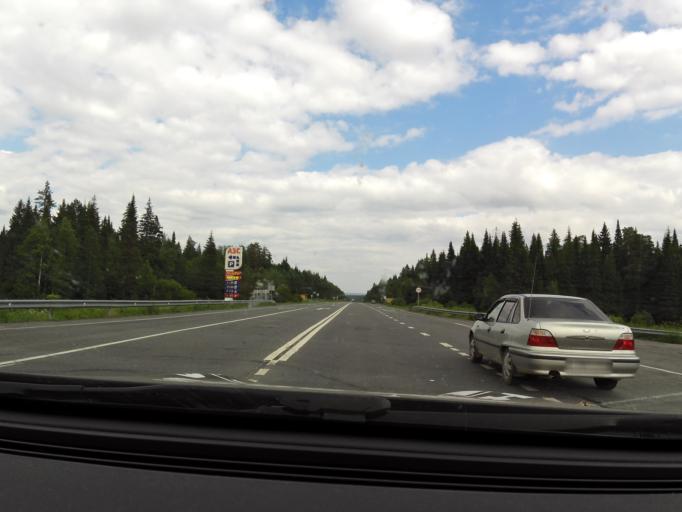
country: RU
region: Sverdlovsk
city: Druzhinino
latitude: 56.7959
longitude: 59.4135
